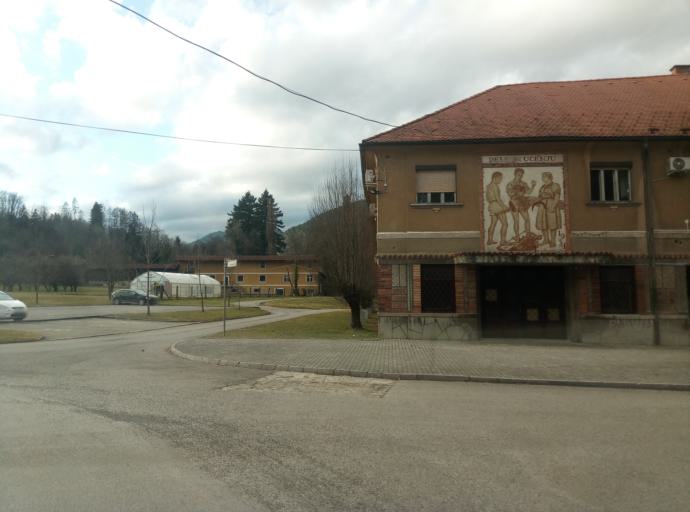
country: SI
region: Radece
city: Radece
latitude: 46.0608
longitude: 15.1901
